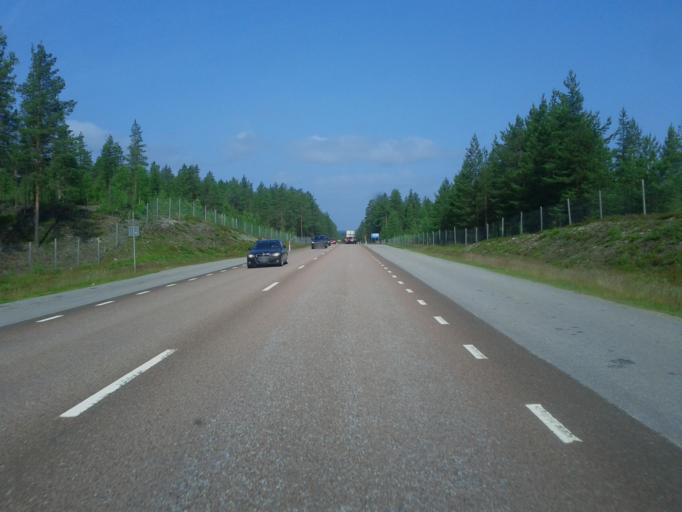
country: SE
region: Vaesterbotten
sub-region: Skelleftea Kommun
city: Burea
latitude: 64.5933
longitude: 21.2112
